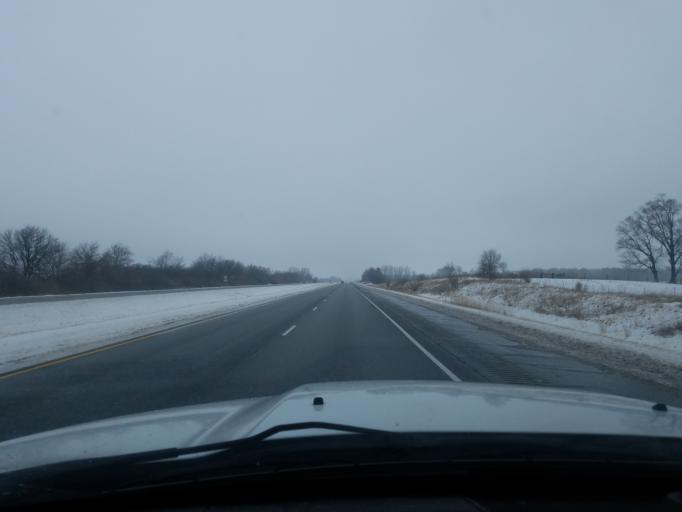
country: US
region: Indiana
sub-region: Fulton County
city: Rochester
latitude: 40.9485
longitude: -86.1683
